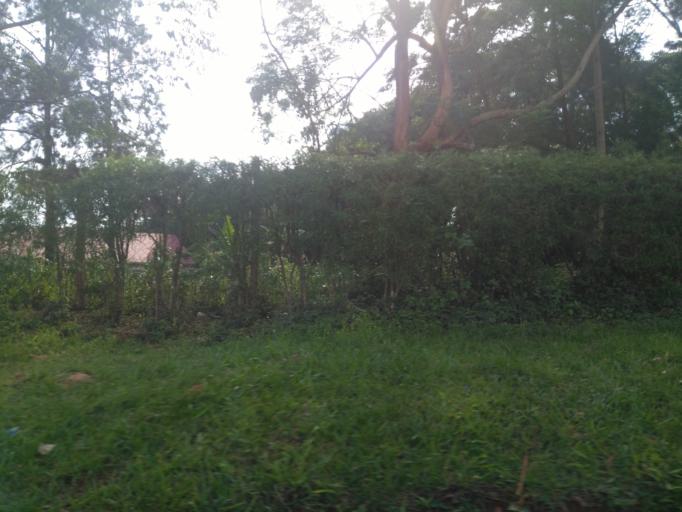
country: UG
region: Eastern Region
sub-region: Jinja District
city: Jinja
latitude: 0.4377
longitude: 33.2100
